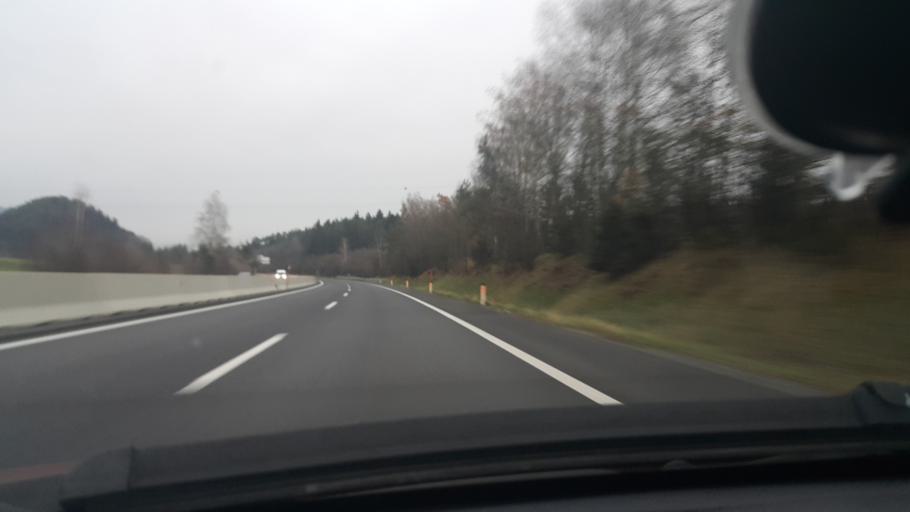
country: AT
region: Carinthia
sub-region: Politischer Bezirk Volkermarkt
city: Voelkermarkt
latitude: 46.6785
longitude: 14.6279
